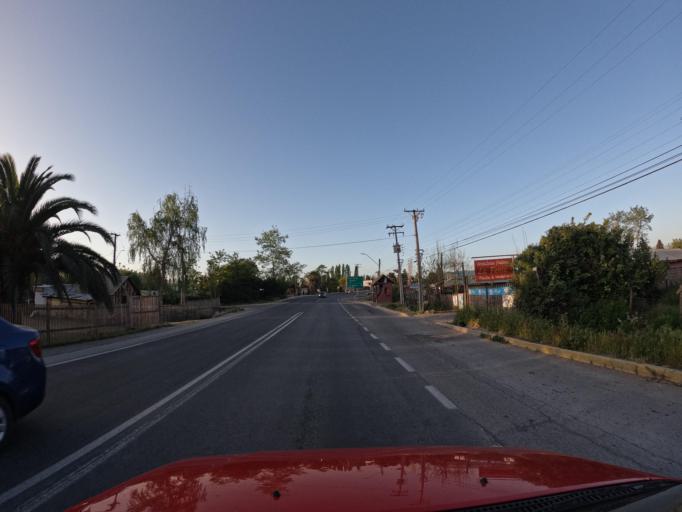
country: CL
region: O'Higgins
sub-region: Provincia de Cachapoal
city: San Vicente
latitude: -34.1685
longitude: -71.3966
